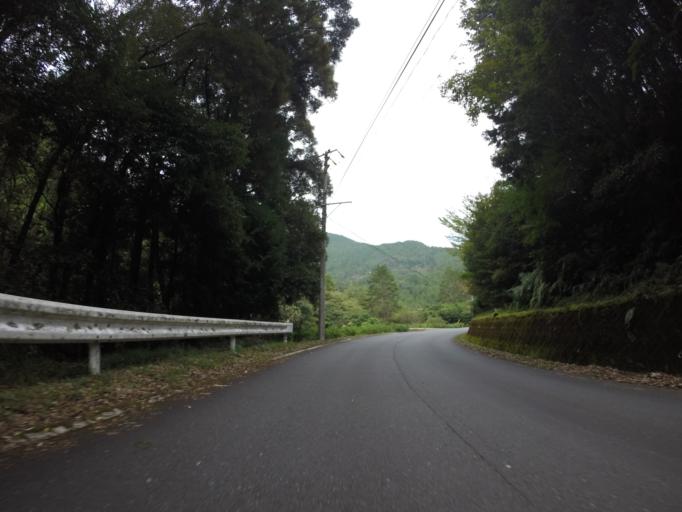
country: JP
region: Shizuoka
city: Mori
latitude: 34.8759
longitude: 138.0212
